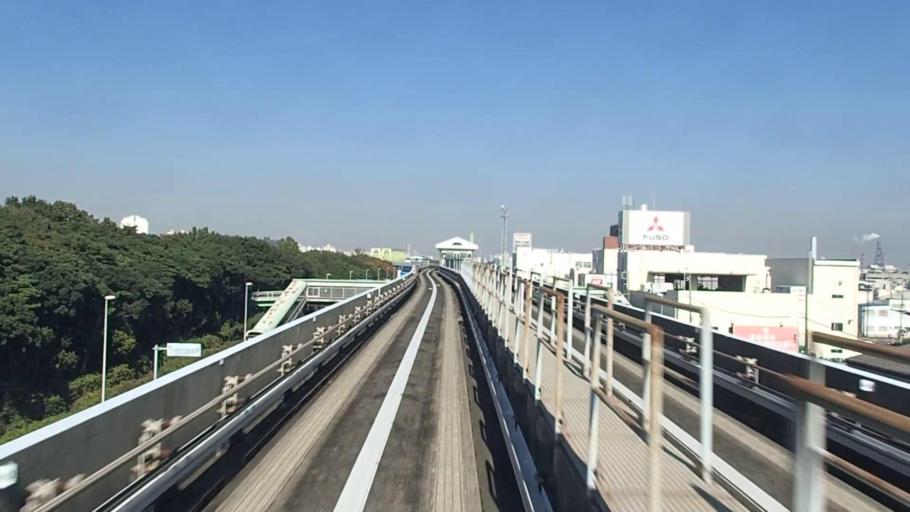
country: JP
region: Kanagawa
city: Yokosuka
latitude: 35.3571
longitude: 139.6438
